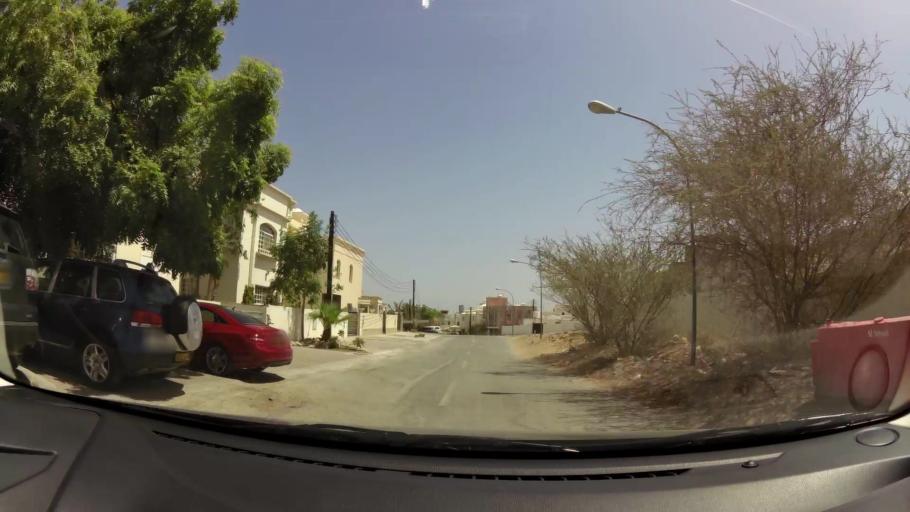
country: OM
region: Muhafazat Masqat
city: Bawshar
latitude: 23.5877
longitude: 58.4499
